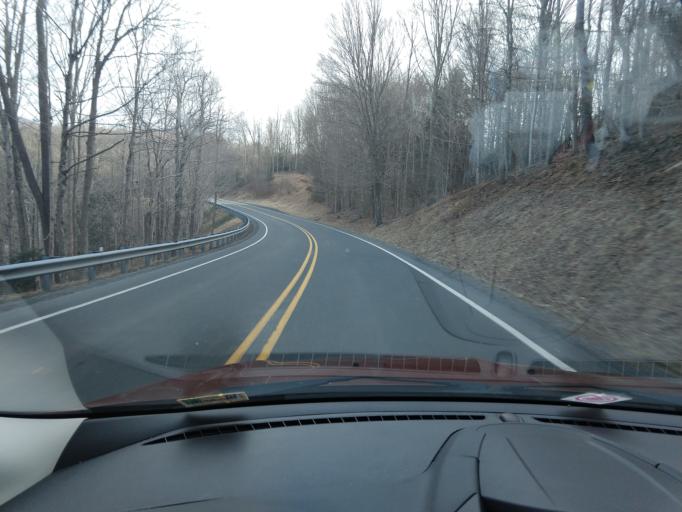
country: US
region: Virginia
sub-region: Highland County
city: Monterey
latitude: 38.4456
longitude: -79.5343
